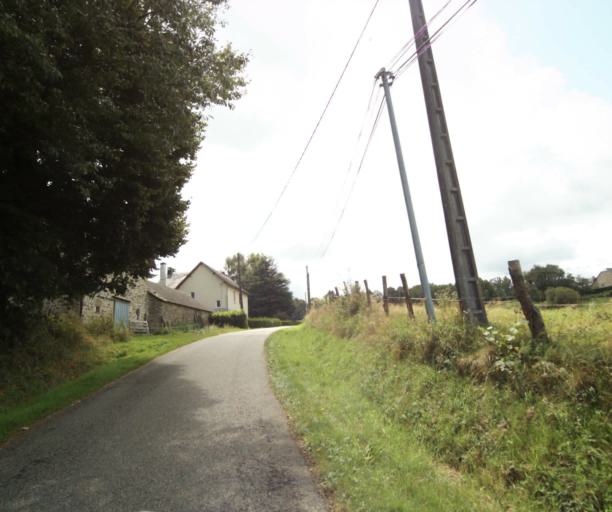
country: FR
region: Limousin
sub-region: Departement de la Correze
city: Sainte-Fortunade
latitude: 45.2020
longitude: 1.8089
